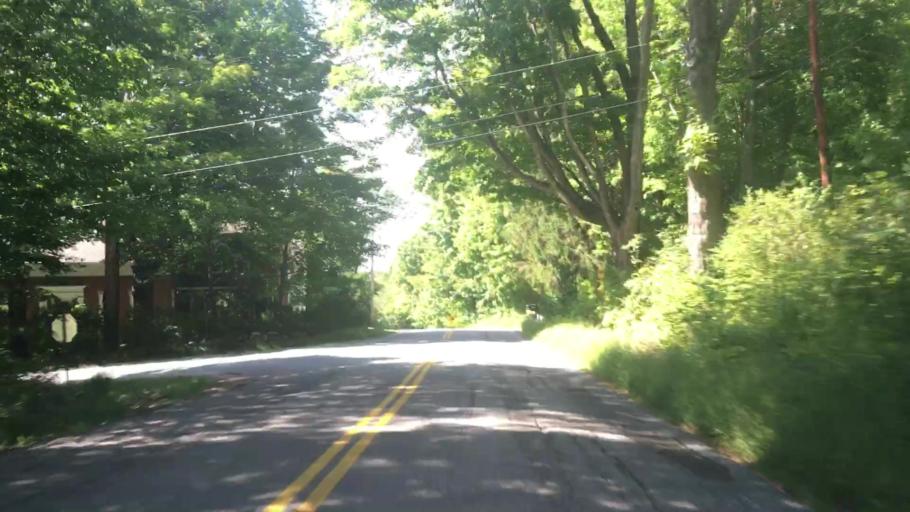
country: US
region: Maine
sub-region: Androscoggin County
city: Poland
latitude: 44.0080
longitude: -70.3760
